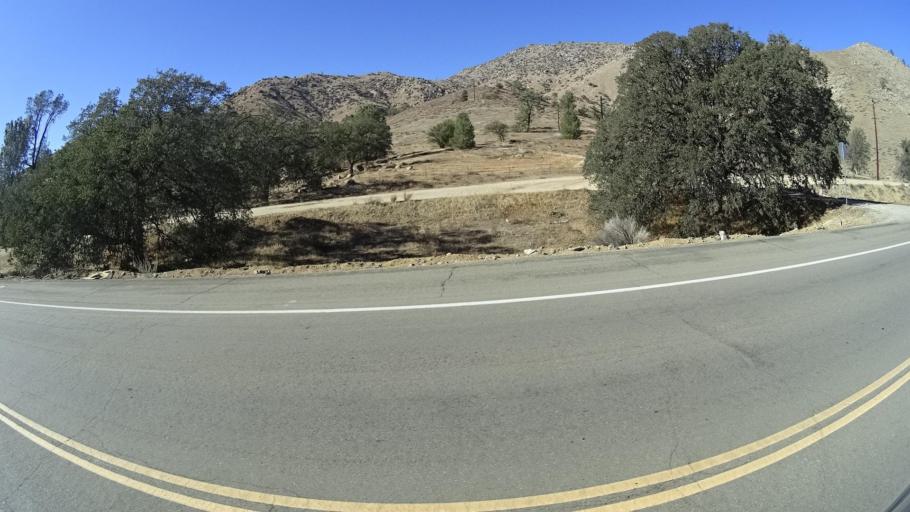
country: US
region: California
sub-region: Kern County
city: Kernville
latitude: 35.7252
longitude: -118.4317
